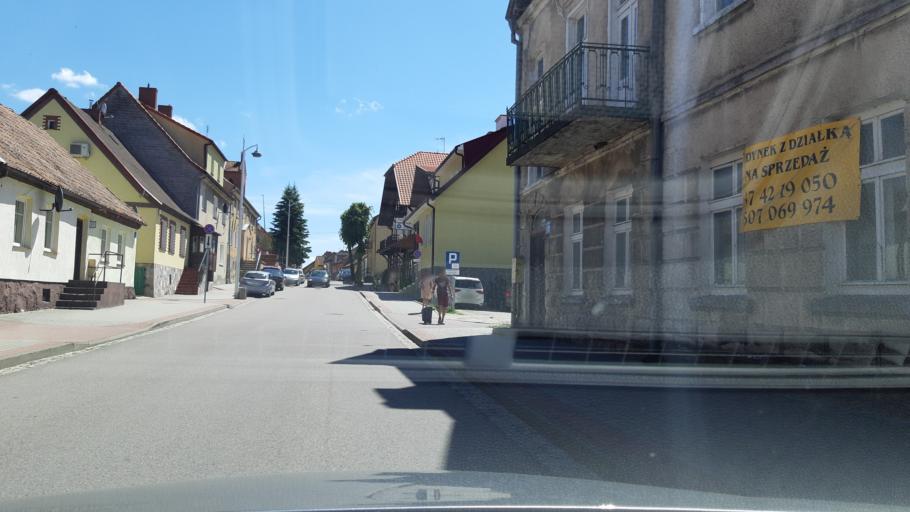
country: PL
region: Warmian-Masurian Voivodeship
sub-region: Powiat mragowski
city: Mikolajki
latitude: 53.7994
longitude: 21.5748
